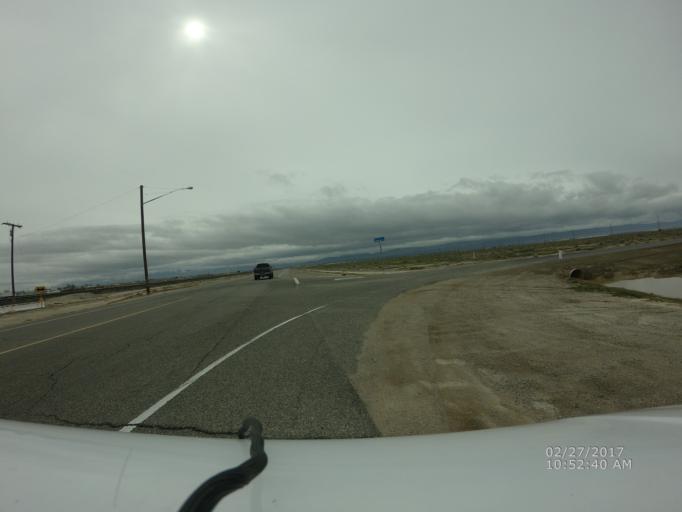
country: US
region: California
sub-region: Los Angeles County
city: Lancaster
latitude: 34.7481
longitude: -118.1446
